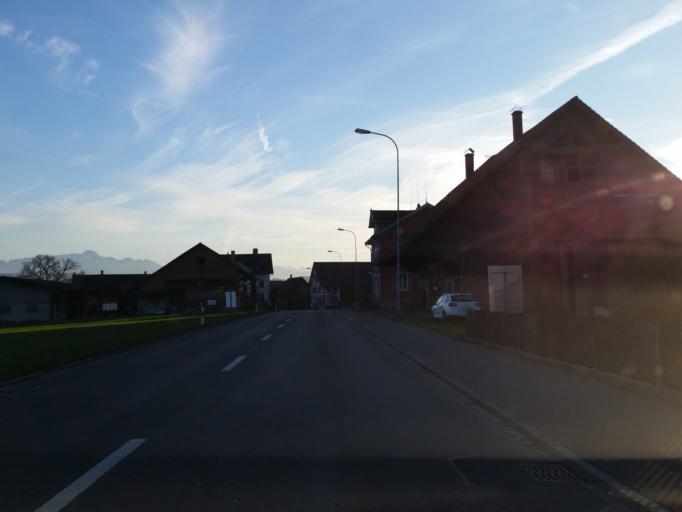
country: CH
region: Thurgau
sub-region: Weinfelden District
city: Erlen
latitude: 47.5255
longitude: 9.2604
